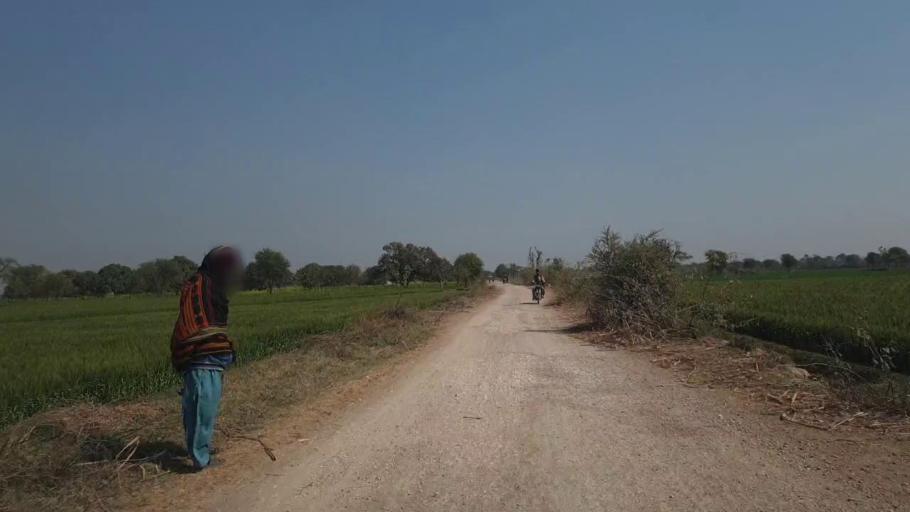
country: PK
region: Sindh
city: Tando Jam
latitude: 25.3116
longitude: 68.6311
